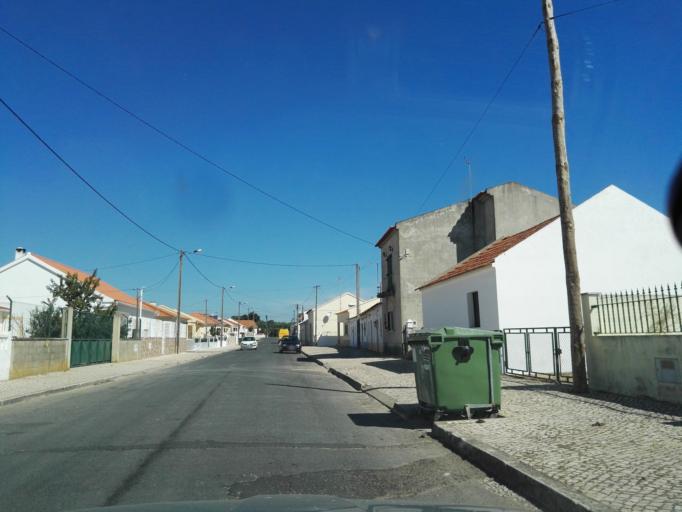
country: PT
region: Santarem
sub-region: Benavente
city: Poceirao
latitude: 38.8642
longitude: -8.7446
